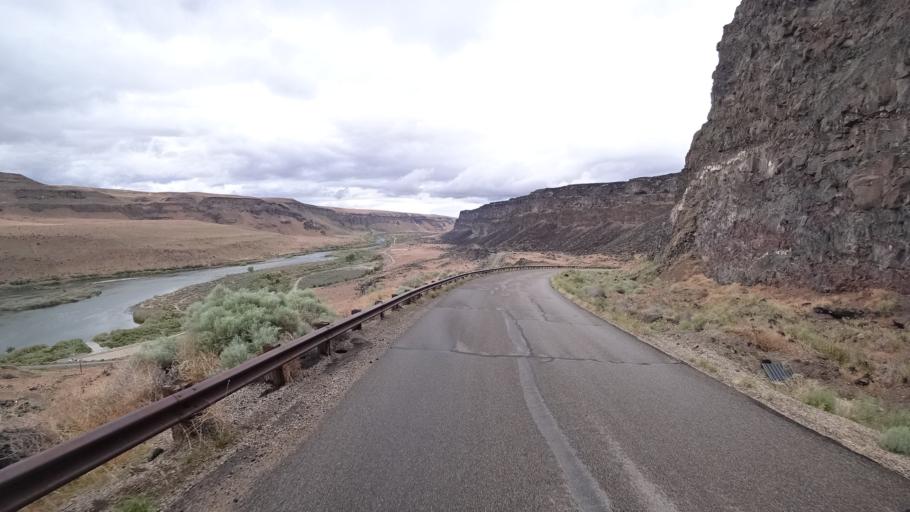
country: US
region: Idaho
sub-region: Owyhee County
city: Murphy
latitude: 43.2458
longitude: -116.3739
